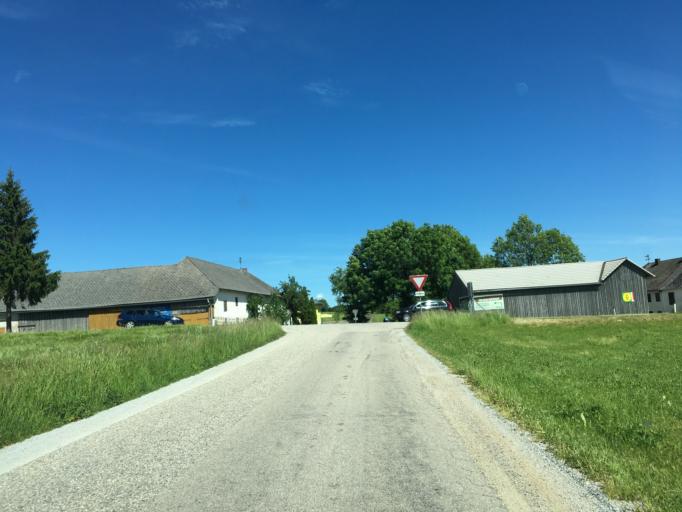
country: AT
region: Upper Austria
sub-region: Politischer Bezirk Urfahr-Umgebung
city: Bad Leonfelden
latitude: 48.5078
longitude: 14.2944
